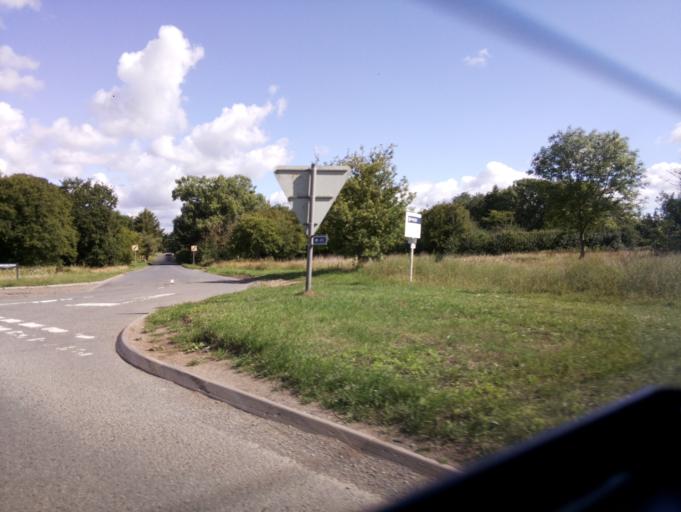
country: GB
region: England
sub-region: Gloucestershire
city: Newent
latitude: 51.9073
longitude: -2.3358
